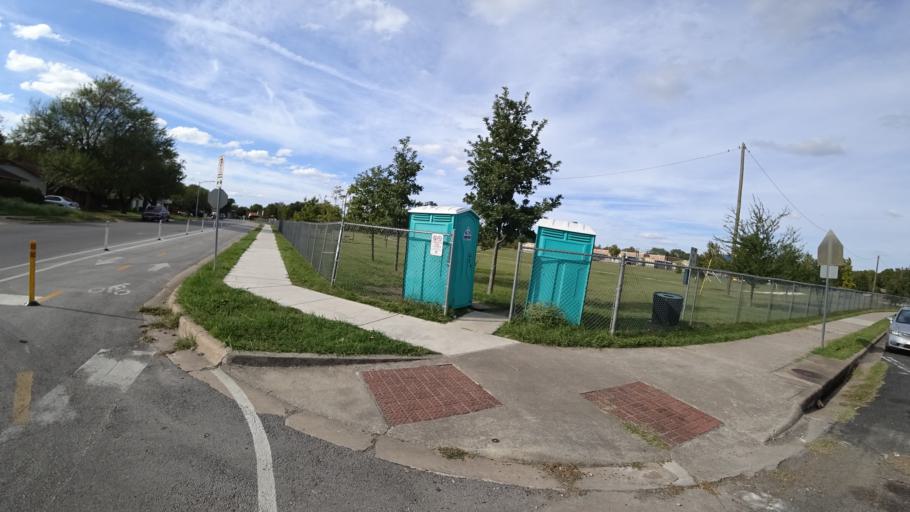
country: US
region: Texas
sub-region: Travis County
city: Onion Creek
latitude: 30.1953
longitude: -97.7555
